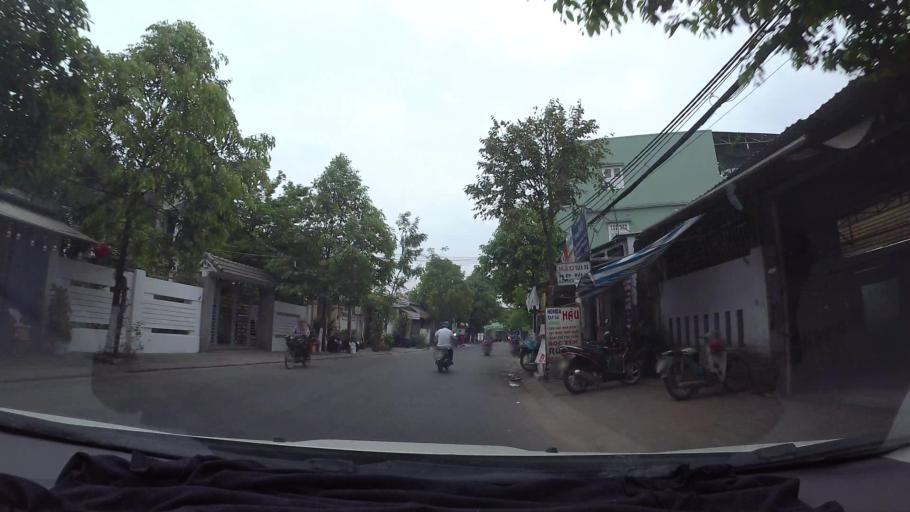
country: VN
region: Da Nang
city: Thanh Khe
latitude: 16.0507
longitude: 108.1803
